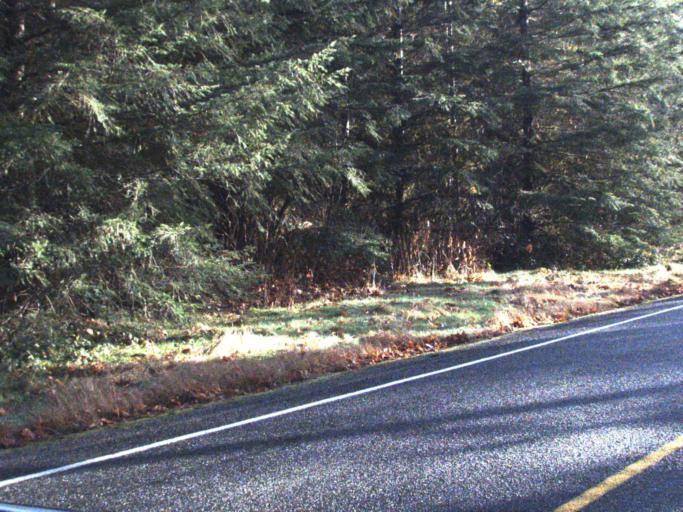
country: US
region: Washington
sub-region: Snohomish County
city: Darrington
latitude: 48.4327
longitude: -121.5710
